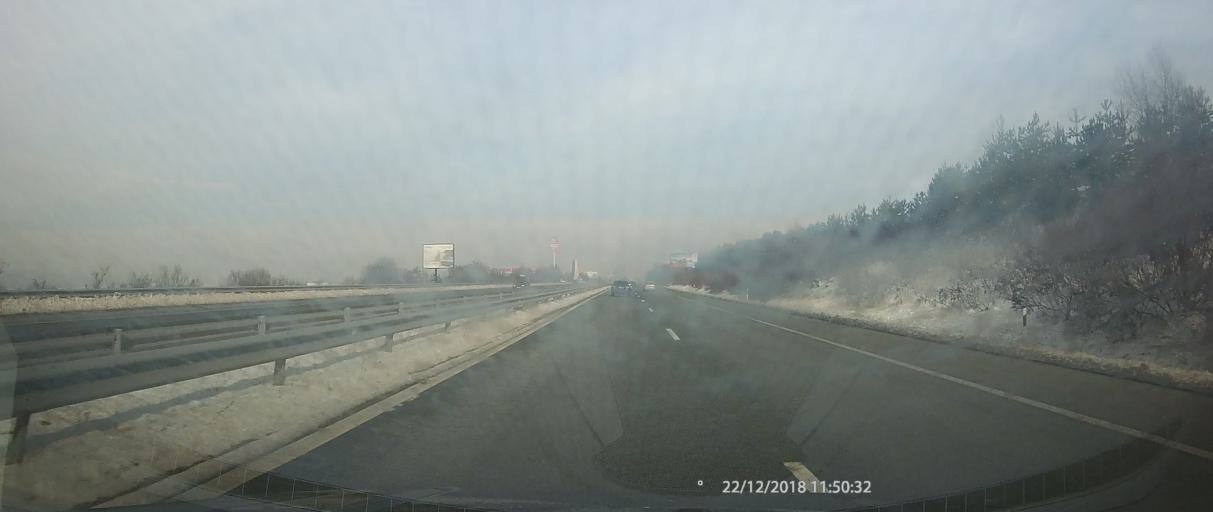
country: BG
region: Pernik
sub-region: Obshtina Pernik
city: Pernik
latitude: 42.5672
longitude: 23.1157
